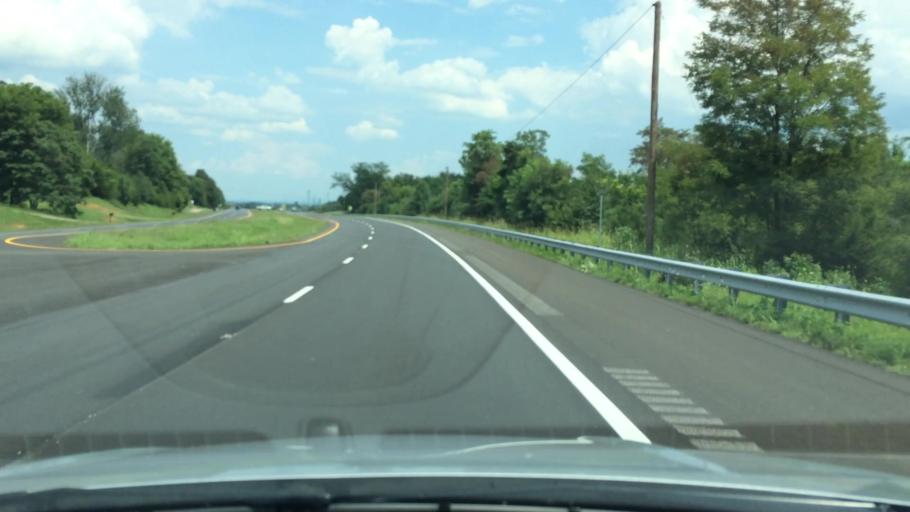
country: US
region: Tennessee
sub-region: Hamblen County
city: Morristown
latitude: 36.1831
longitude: -83.2526
